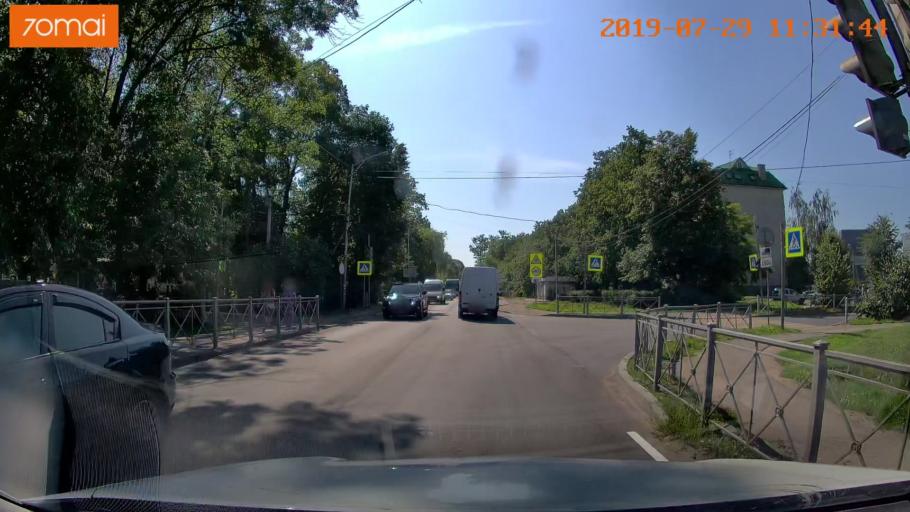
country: RU
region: Kaliningrad
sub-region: Gorod Kaliningrad
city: Kaliningrad
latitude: 54.6741
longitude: 20.5426
